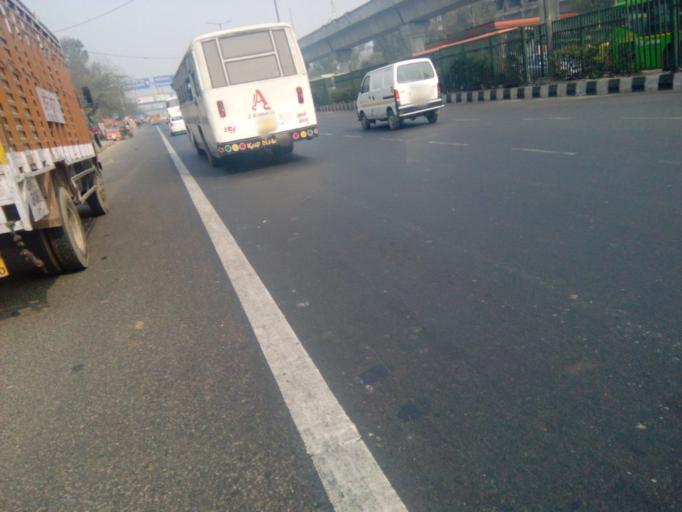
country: IN
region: Uttar Pradesh
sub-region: Gautam Buddha Nagar
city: Noida
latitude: 28.6433
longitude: 77.3163
